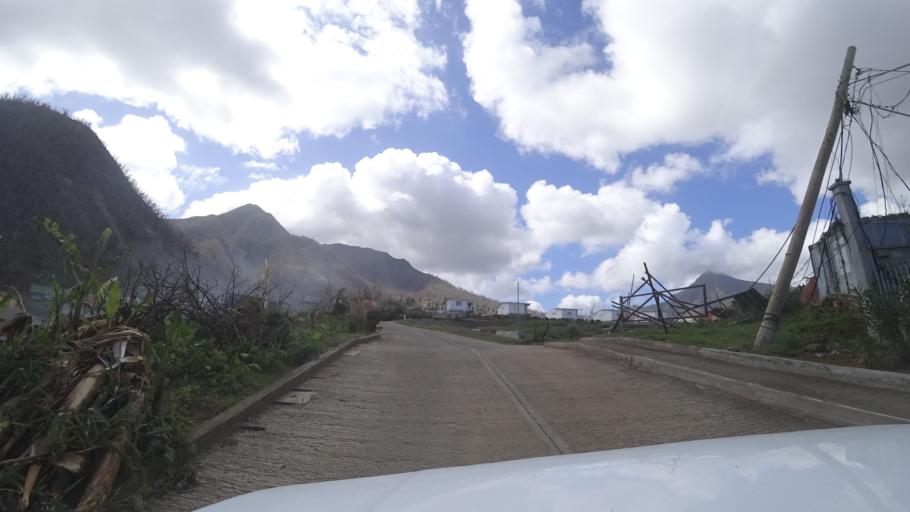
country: DM
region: Saint Patrick
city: Berekua
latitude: 15.2447
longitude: -61.3226
